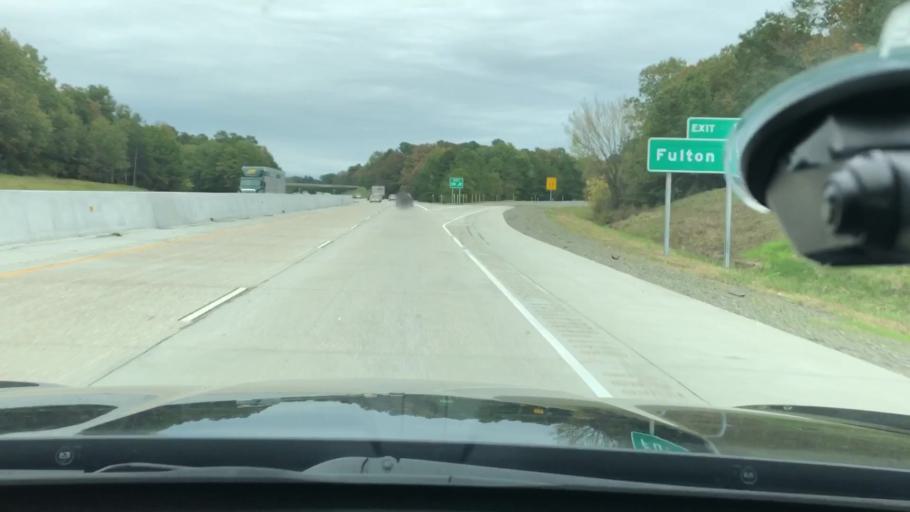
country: US
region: Arkansas
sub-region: Hempstead County
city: Hope
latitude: 33.6086
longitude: -93.8035
